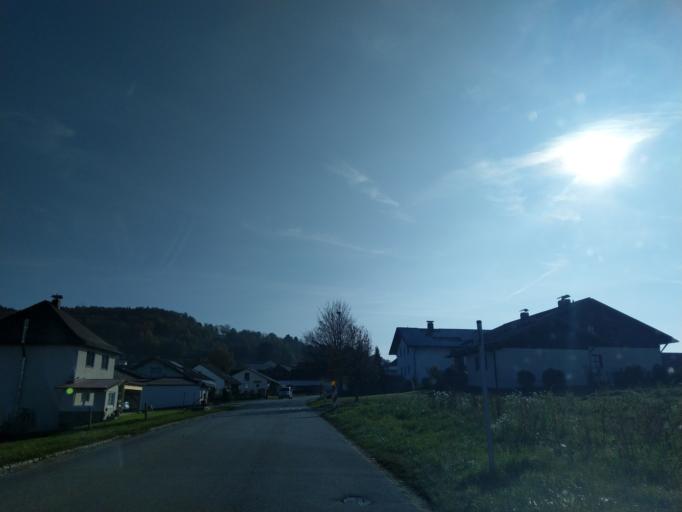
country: DE
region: Bavaria
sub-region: Lower Bavaria
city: Grattersdorf
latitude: 48.8064
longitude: 13.1482
